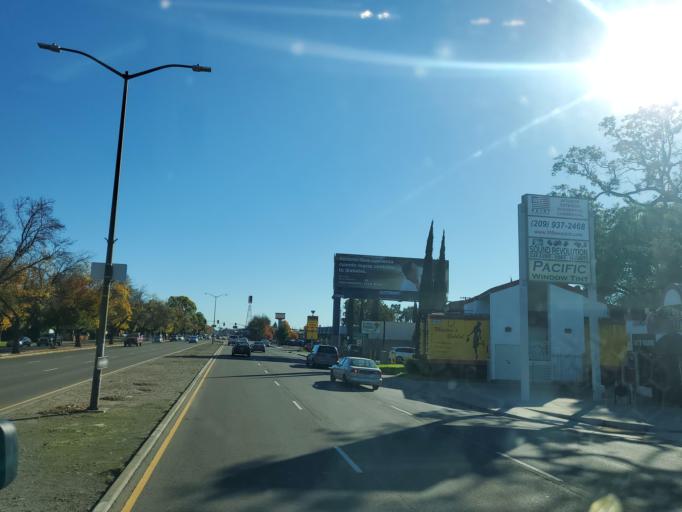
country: US
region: California
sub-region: San Joaquin County
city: Lincoln Village
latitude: 38.0156
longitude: -121.3224
